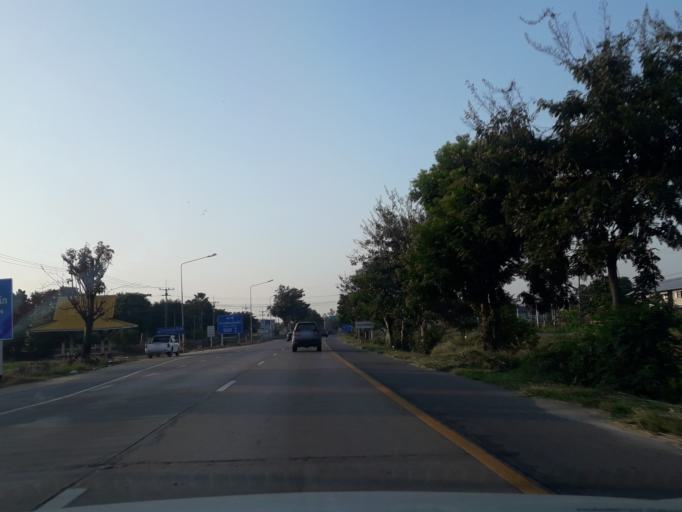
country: TH
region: Phra Nakhon Si Ayutthaya
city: Phra Nakhon Si Ayutthaya
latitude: 14.3196
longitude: 100.5277
